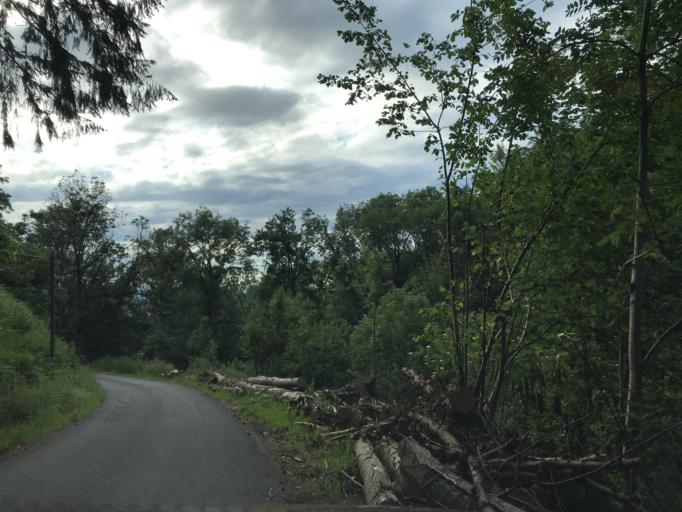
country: FR
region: Auvergne
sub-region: Departement du Puy-de-Dome
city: Thiers
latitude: 45.8522
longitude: 3.5607
